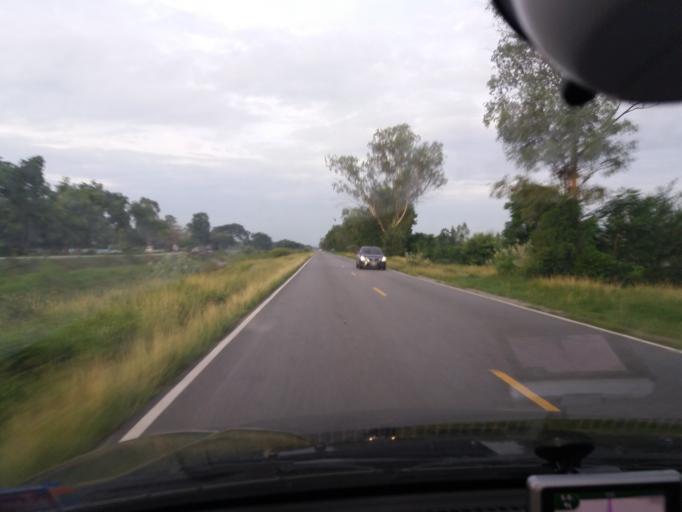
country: TH
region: Suphan Buri
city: Don Chedi
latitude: 14.5483
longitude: 99.9421
